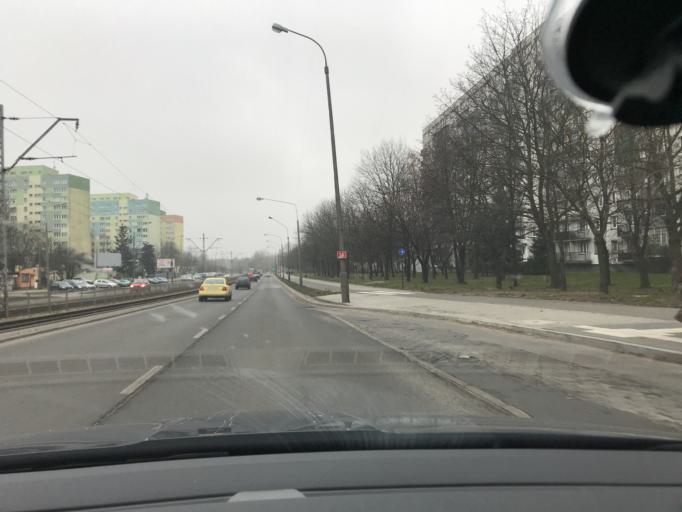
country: PL
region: Lodz Voivodeship
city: Lodz
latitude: 51.7287
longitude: 19.4696
